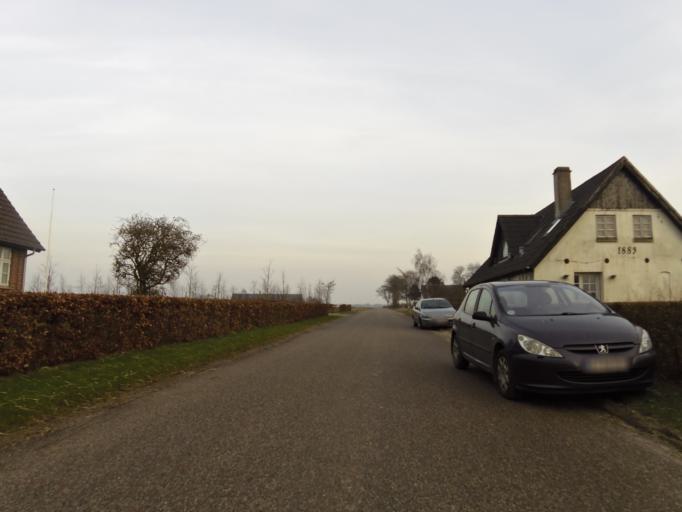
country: DK
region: South Denmark
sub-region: Haderslev Kommune
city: Gram
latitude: 55.3481
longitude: 8.9410
